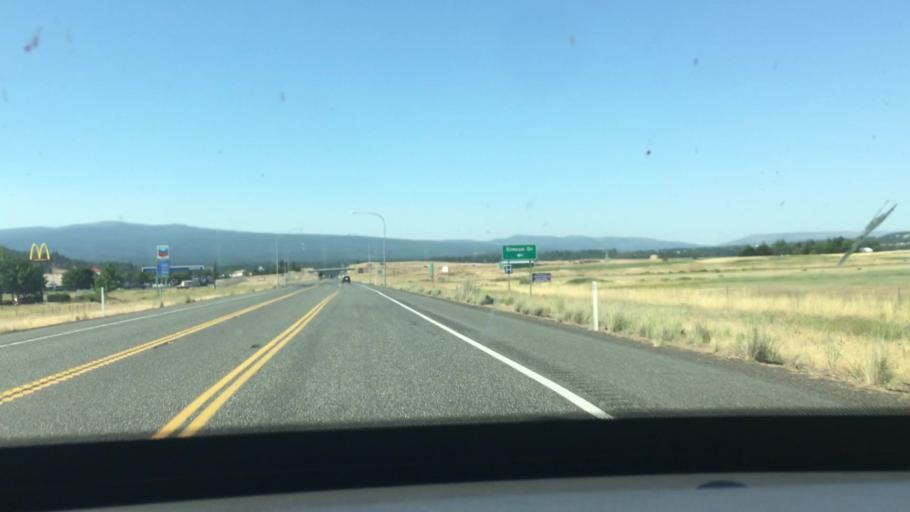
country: US
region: Washington
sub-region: Klickitat County
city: Goldendale
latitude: 45.8105
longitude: -120.8076
